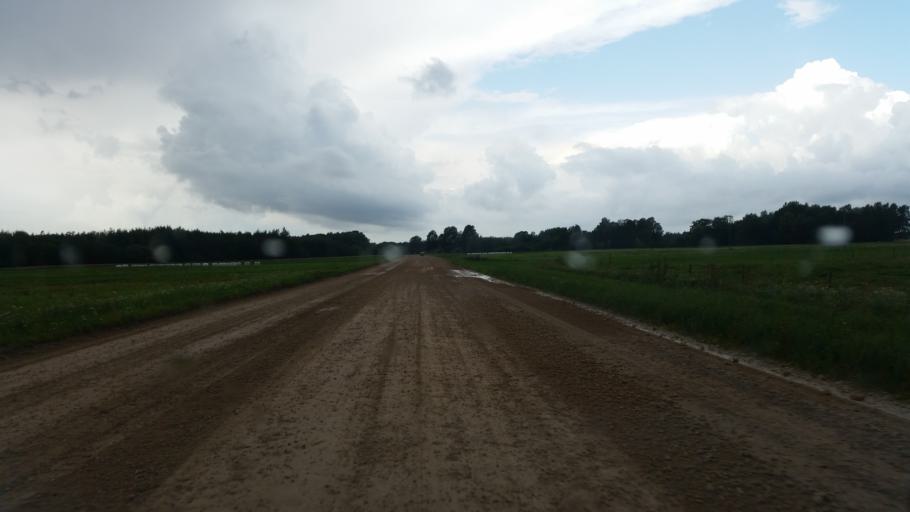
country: LV
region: Vecumnieki
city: Vecumnieki
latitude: 56.4294
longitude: 24.4580
